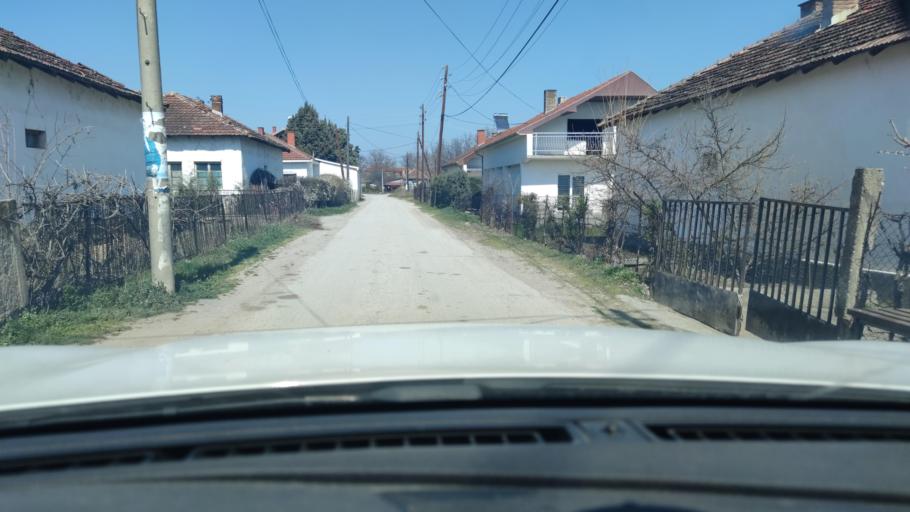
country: MK
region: Rosoman
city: Rosoman
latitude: 41.5193
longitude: 21.9411
